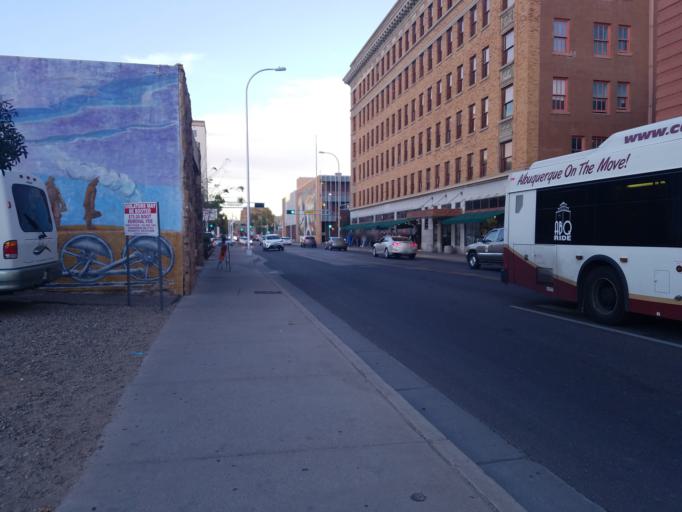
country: US
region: New Mexico
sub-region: Bernalillo County
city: Albuquerque
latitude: 35.0835
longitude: -106.6494
